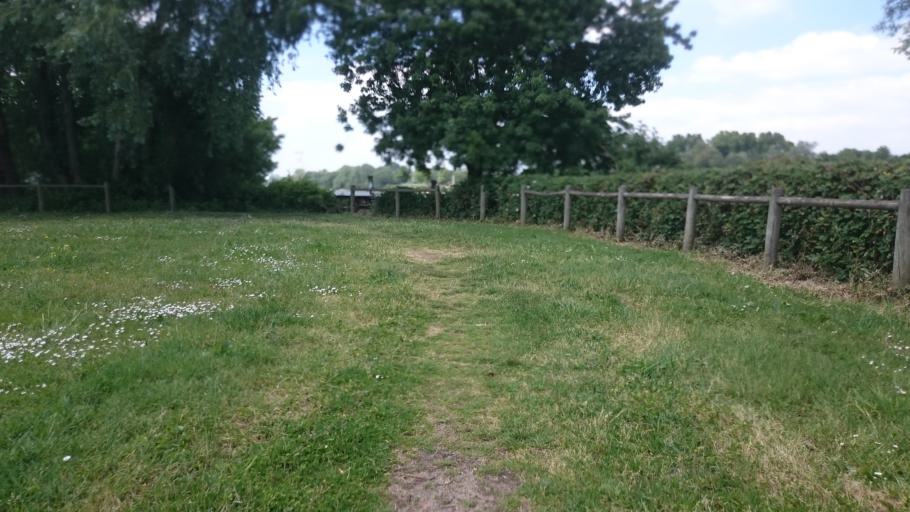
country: FR
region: Pays de la Loire
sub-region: Departement de la Loire-Atlantique
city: Bouguenais
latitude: 47.1906
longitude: -1.6421
